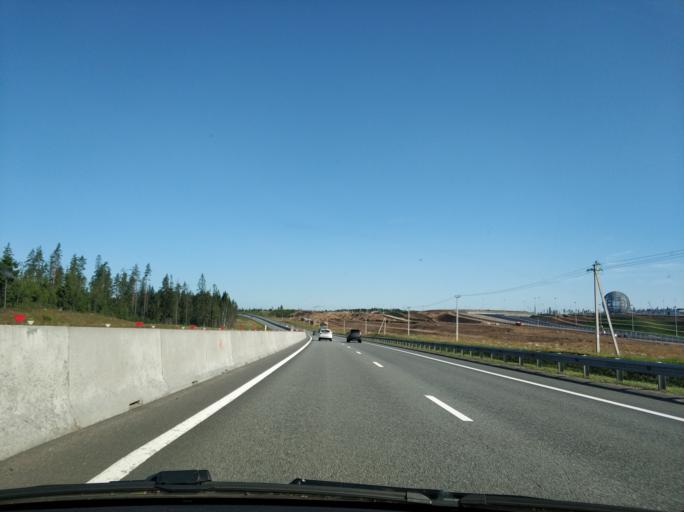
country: RU
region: Leningrad
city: Sosnovo
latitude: 60.5052
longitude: 30.1935
